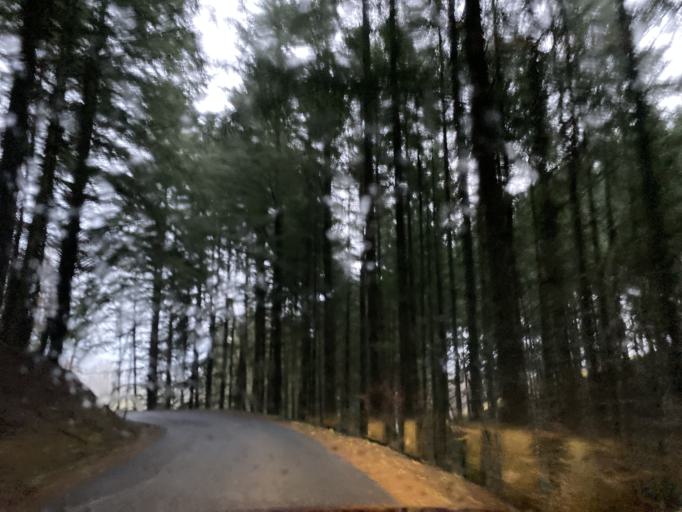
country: FR
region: Auvergne
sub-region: Departement du Puy-de-Dome
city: La Monnerie-le-Montel
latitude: 45.8460
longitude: 3.6068
